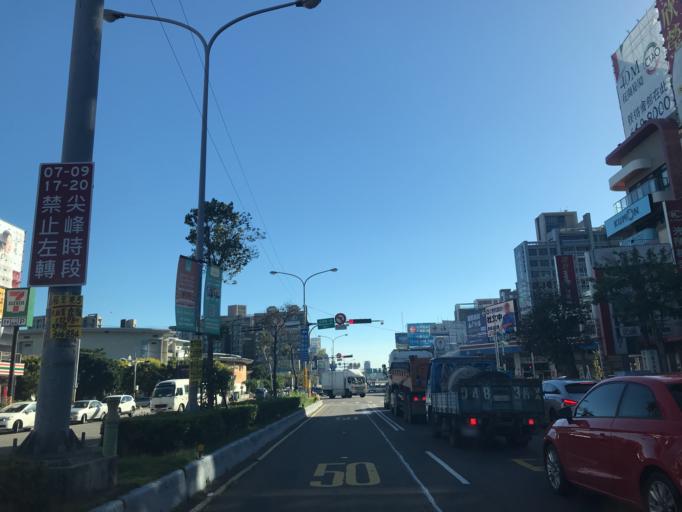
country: TW
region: Taiwan
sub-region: Hsinchu
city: Zhubei
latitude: 24.8139
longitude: 121.0236
